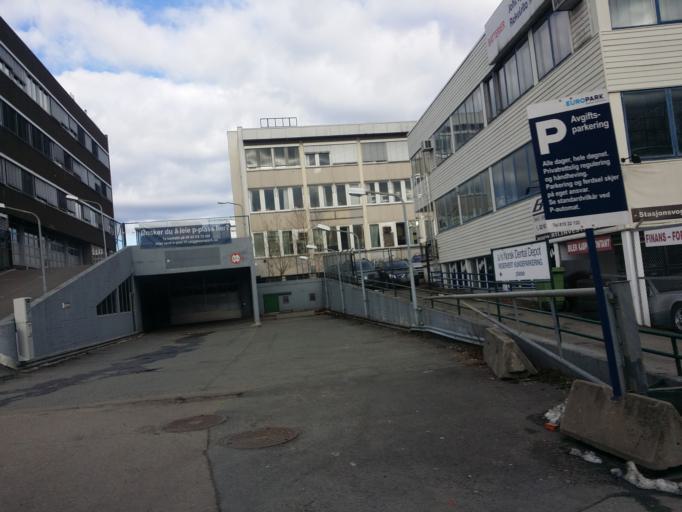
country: NO
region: Oslo
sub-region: Oslo
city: Oslo
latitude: 59.9100
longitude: 10.8136
